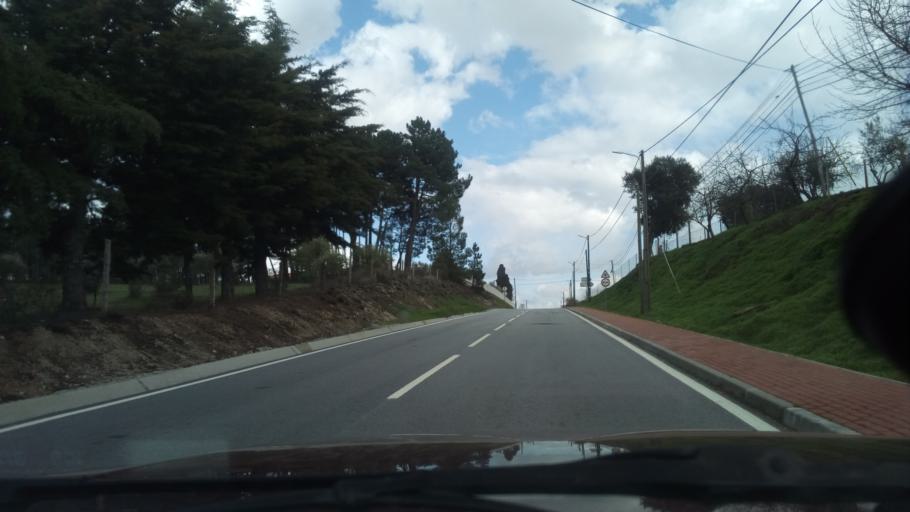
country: PT
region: Guarda
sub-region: Celorico da Beira
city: Celorico da Beira
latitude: 40.6406
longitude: -7.3775
